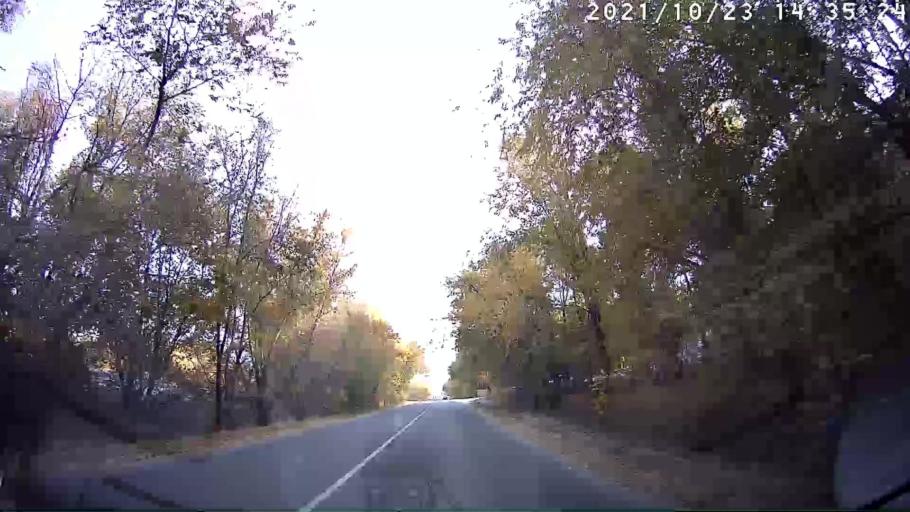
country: RU
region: Volgograd
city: Krasnoslobodsk
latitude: 48.5082
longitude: 44.5303
